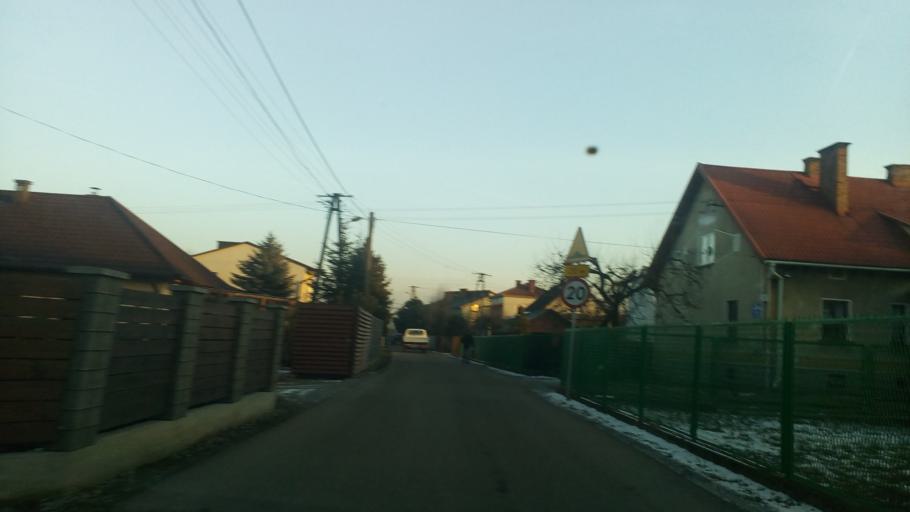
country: PL
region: Lesser Poland Voivodeship
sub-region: Powiat nowosadecki
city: Chelmiec
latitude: 49.6295
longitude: 20.6654
